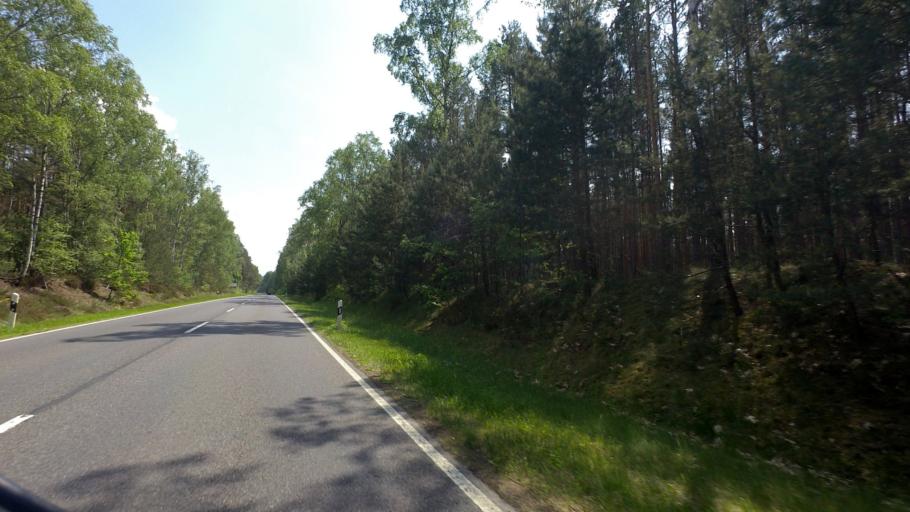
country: DE
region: Saxony
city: Schleife
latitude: 51.5553
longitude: 14.5009
